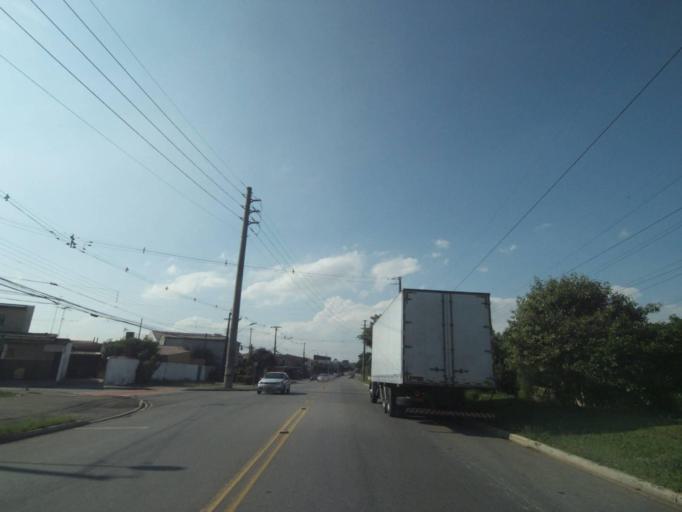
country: BR
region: Parana
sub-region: Araucaria
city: Araucaria
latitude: -25.5329
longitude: -49.3311
